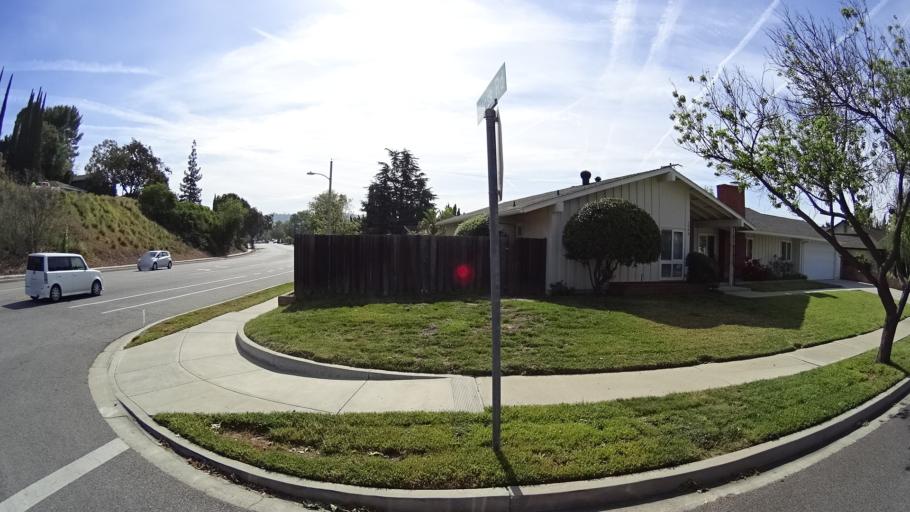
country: US
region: California
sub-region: Ventura County
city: Thousand Oaks
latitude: 34.2000
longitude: -118.8732
